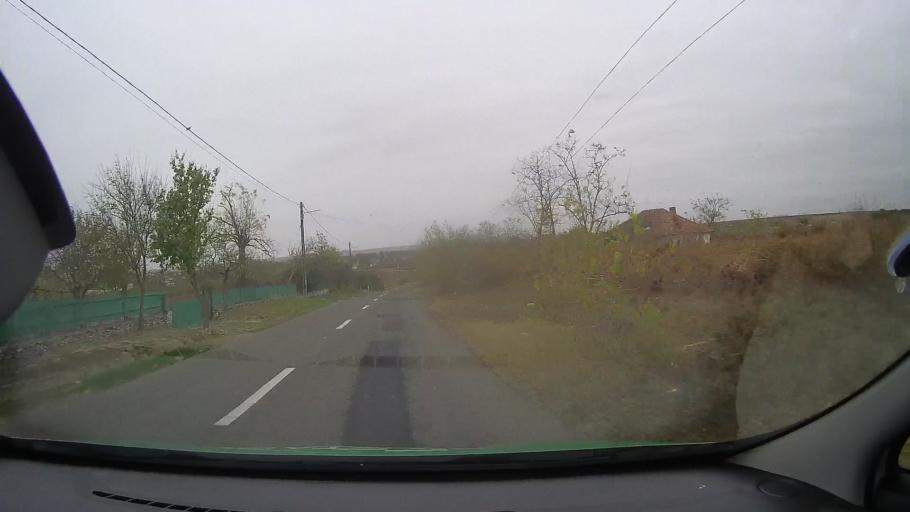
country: RO
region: Constanta
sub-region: Comuna Vulturu
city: Vulturu
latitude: 44.6984
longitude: 28.2409
